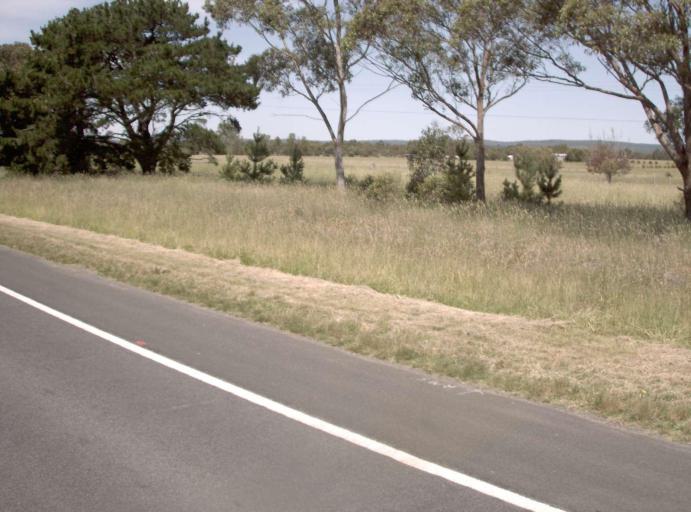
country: AU
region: Victoria
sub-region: Wellington
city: Heyfield
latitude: -38.1562
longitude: 146.7550
